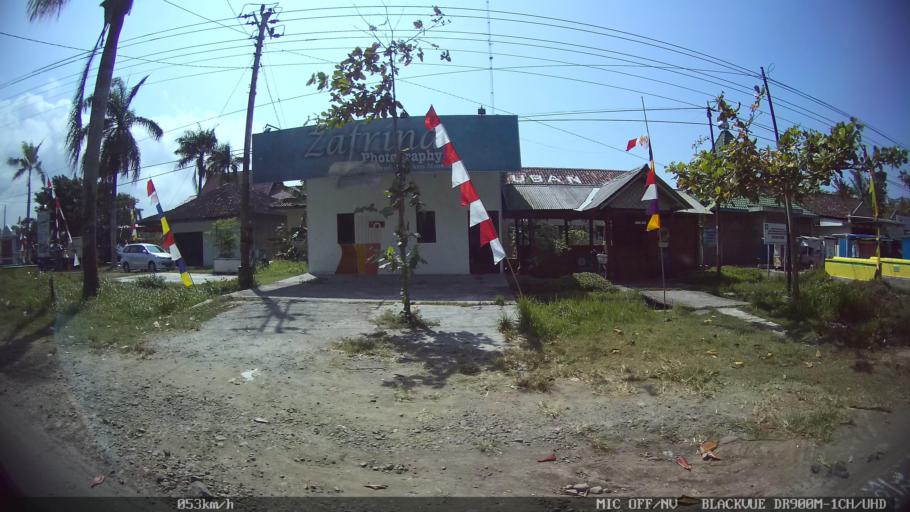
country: ID
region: Daerah Istimewa Yogyakarta
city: Srandakan
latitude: -7.9058
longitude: 110.1523
